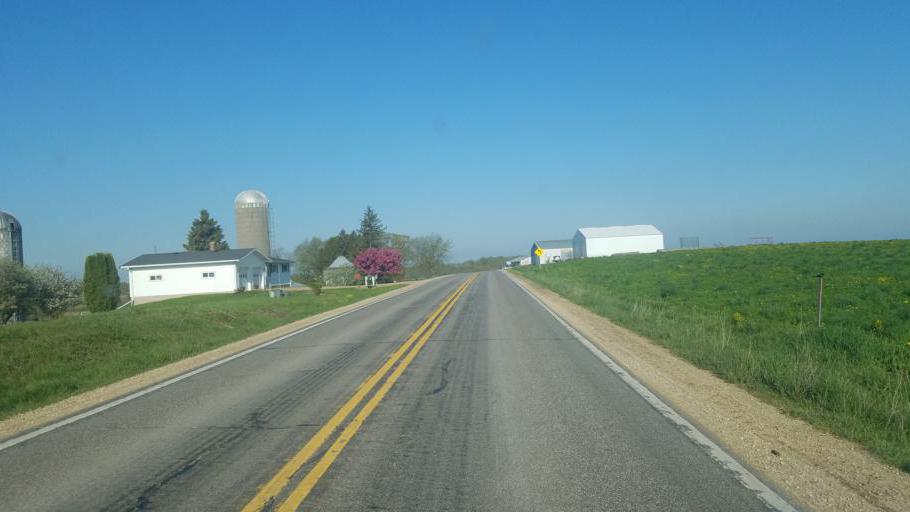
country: US
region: Wisconsin
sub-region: Vernon County
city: Hillsboro
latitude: 43.5952
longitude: -90.4850
